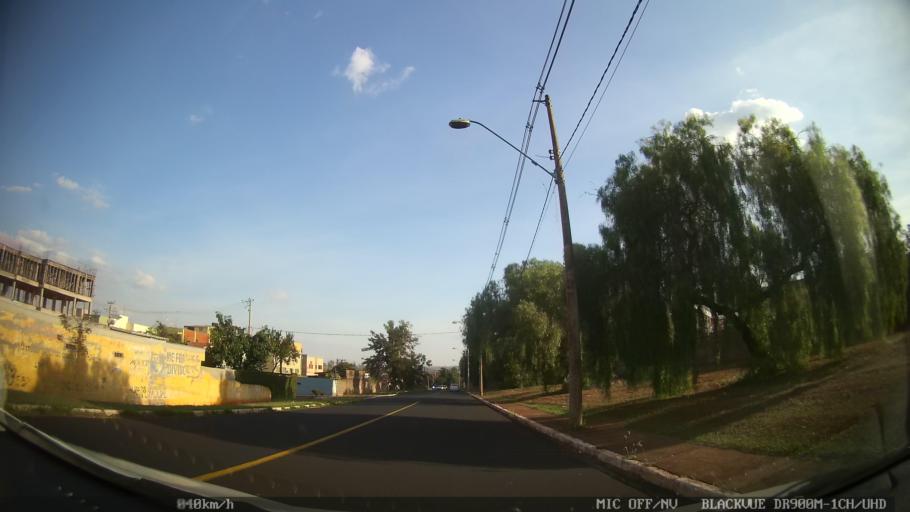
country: BR
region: Sao Paulo
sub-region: Ribeirao Preto
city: Ribeirao Preto
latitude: -21.1655
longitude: -47.8450
